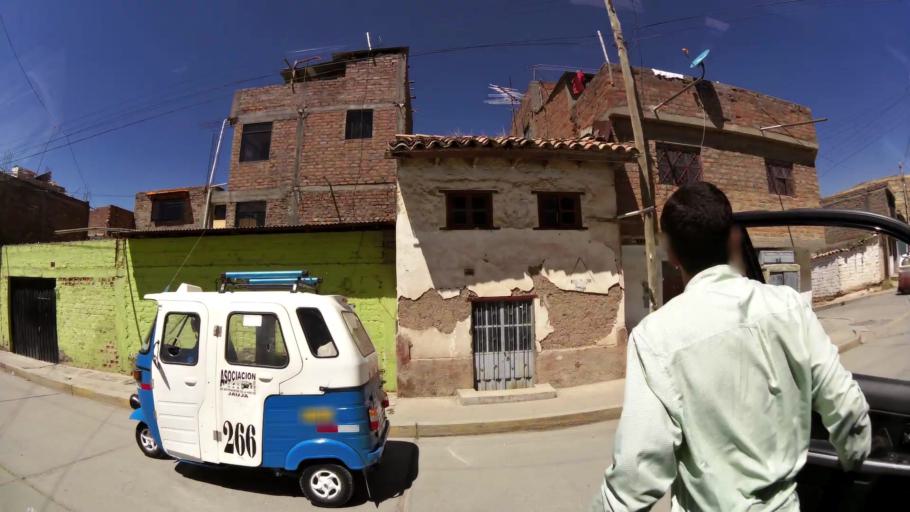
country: PE
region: Junin
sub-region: Provincia de Jauja
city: Jauja
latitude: -11.7774
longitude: -75.5013
